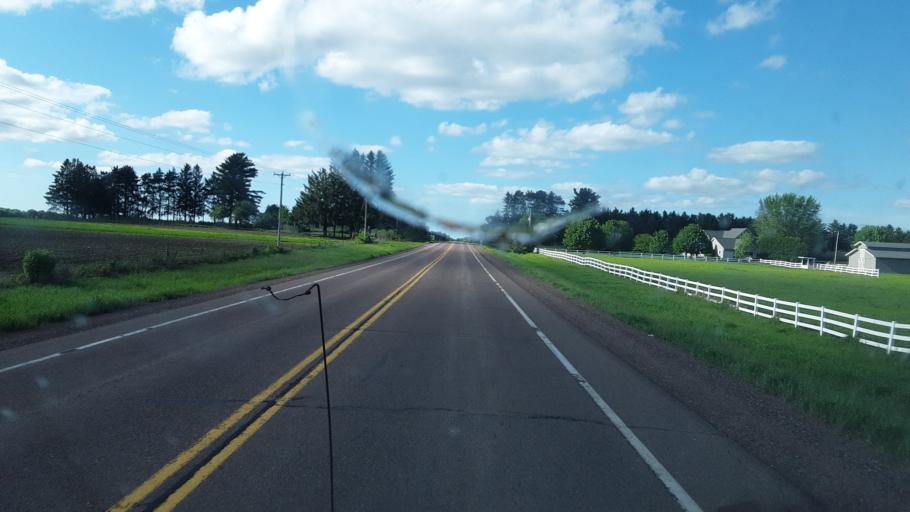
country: US
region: Wisconsin
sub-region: Wood County
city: Marshfield
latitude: 44.5442
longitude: -90.1803
